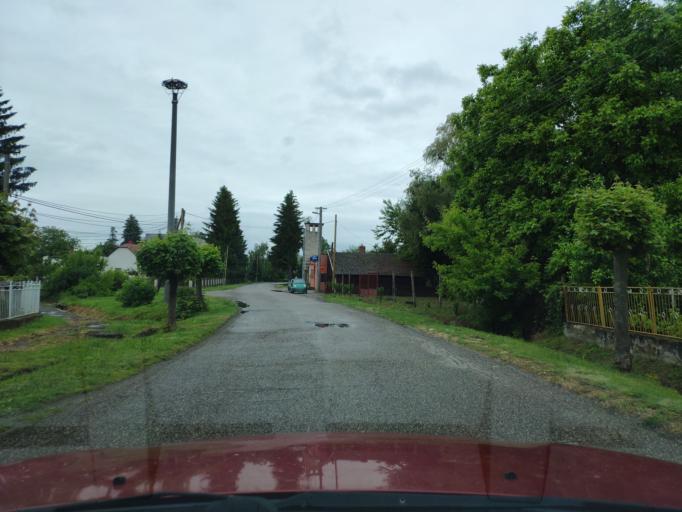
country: HU
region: Borsod-Abauj-Zemplen
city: Karcsa
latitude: 48.3998
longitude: 21.8085
